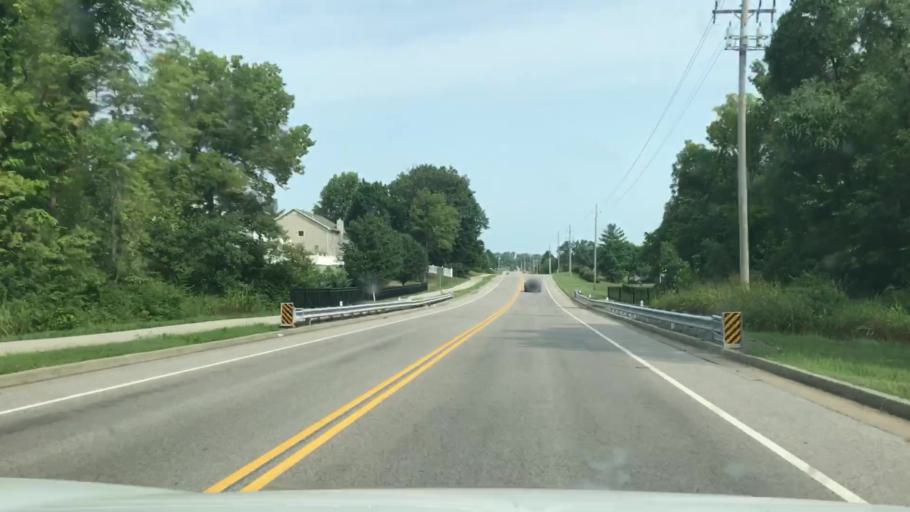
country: US
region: Missouri
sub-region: Saint Charles County
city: Cottleville
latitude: 38.7213
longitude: -90.6425
